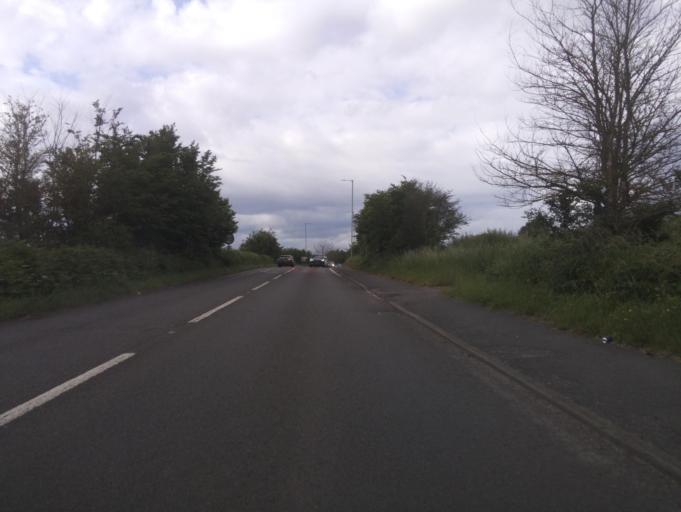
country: GB
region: England
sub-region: Dudley
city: Kingswinford
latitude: 52.4935
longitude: -2.1888
